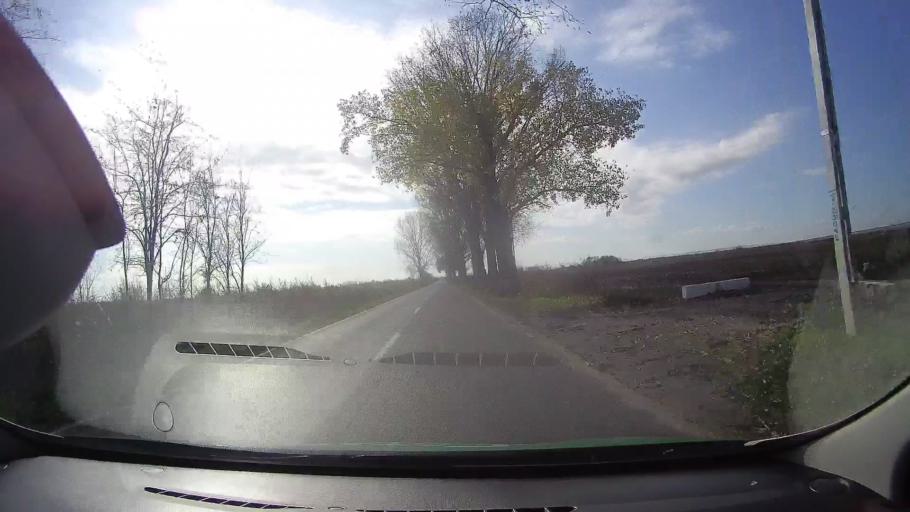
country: RO
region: Tulcea
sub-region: Comuna Valea Nucarilor
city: Agighiol
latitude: 44.9882
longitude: 28.8849
